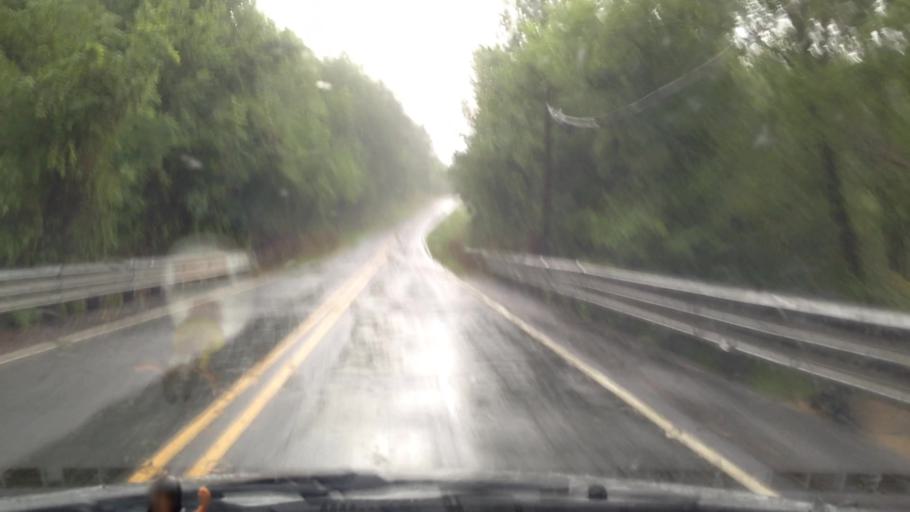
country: US
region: North Carolina
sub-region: Guilford County
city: Stokesdale
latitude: 36.2250
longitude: -80.0306
